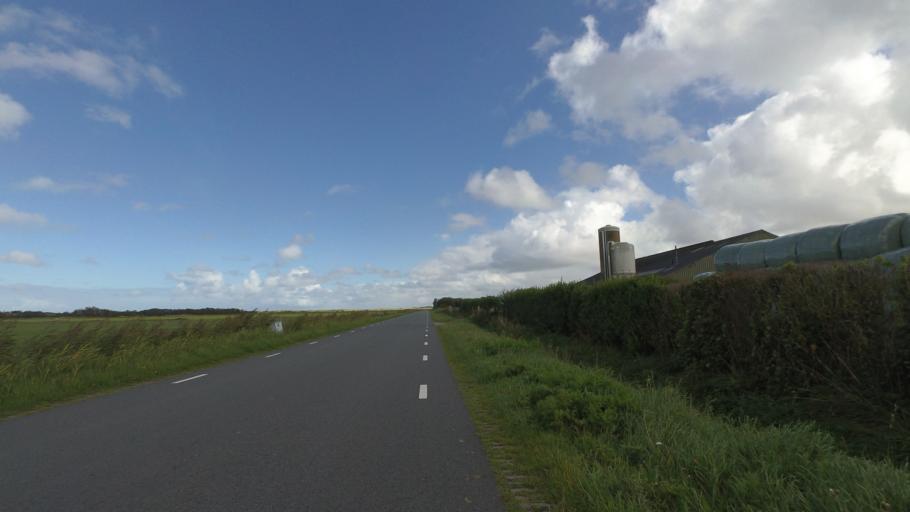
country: NL
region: Friesland
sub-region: Gemeente Ameland
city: Nes
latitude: 53.4492
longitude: 5.8133
